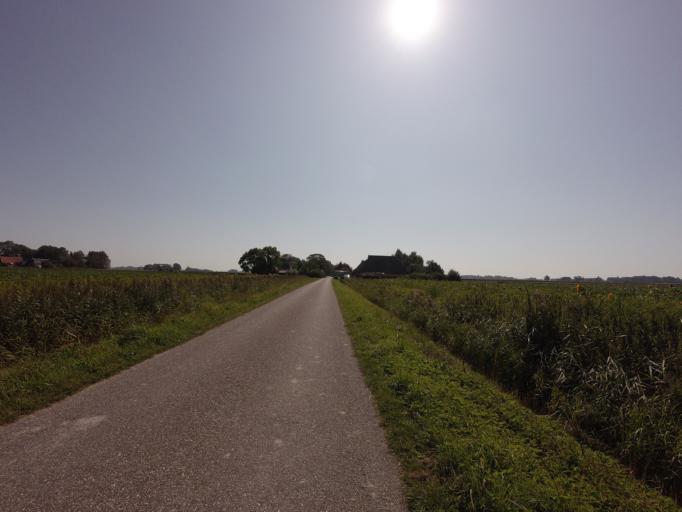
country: NL
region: Friesland
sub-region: Gemeente Dongeradeel
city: Holwerd
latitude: 53.3683
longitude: 5.9215
